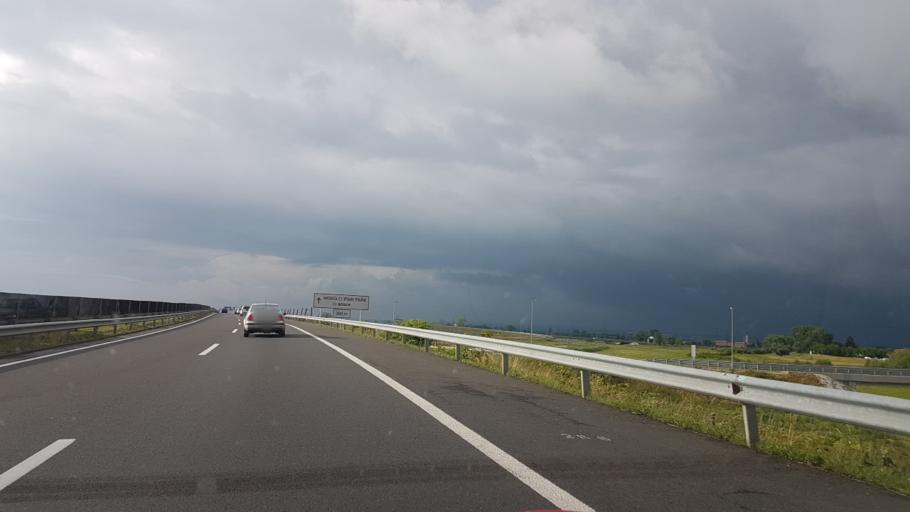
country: HU
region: Borsod-Abauj-Zemplen
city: Felsozsolca
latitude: 48.1059
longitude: 20.8453
